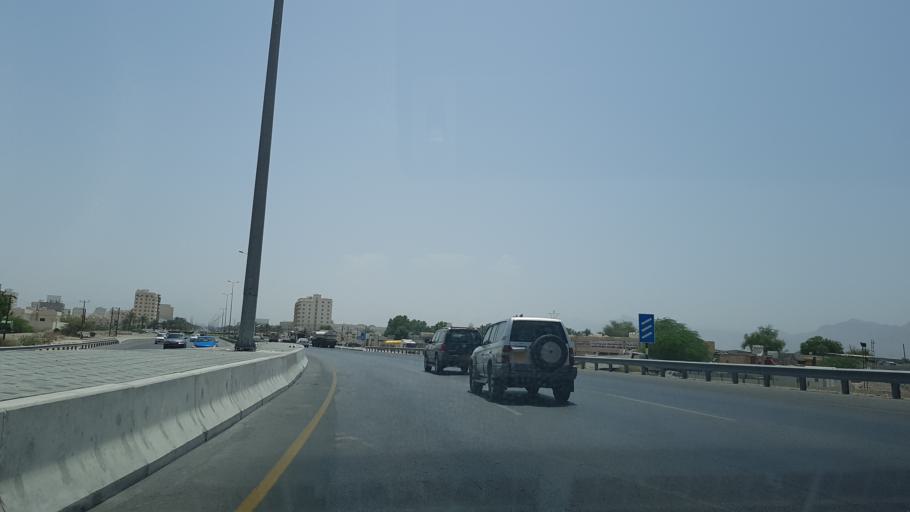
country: OM
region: Muhafazat Masqat
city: Muscat
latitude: 23.5382
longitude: 58.5133
